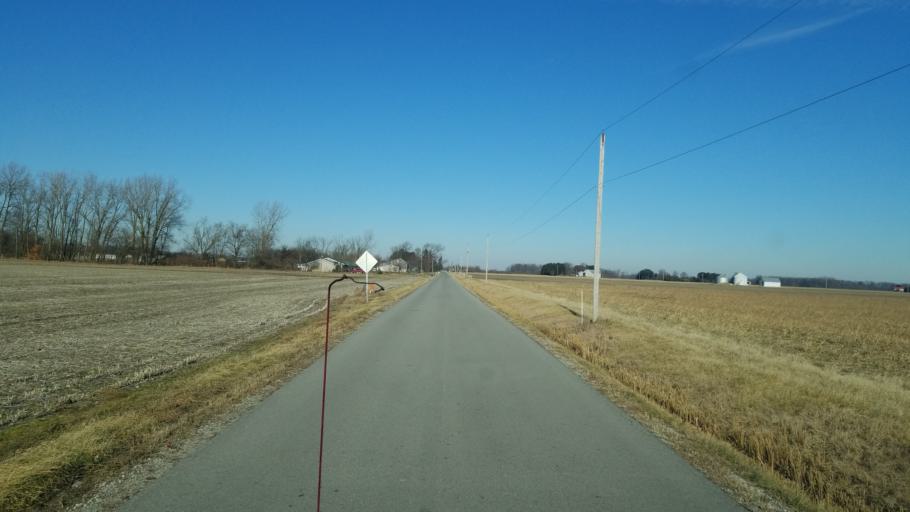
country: US
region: Ohio
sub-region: Henry County
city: Liberty Center
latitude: 41.3731
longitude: -83.9705
